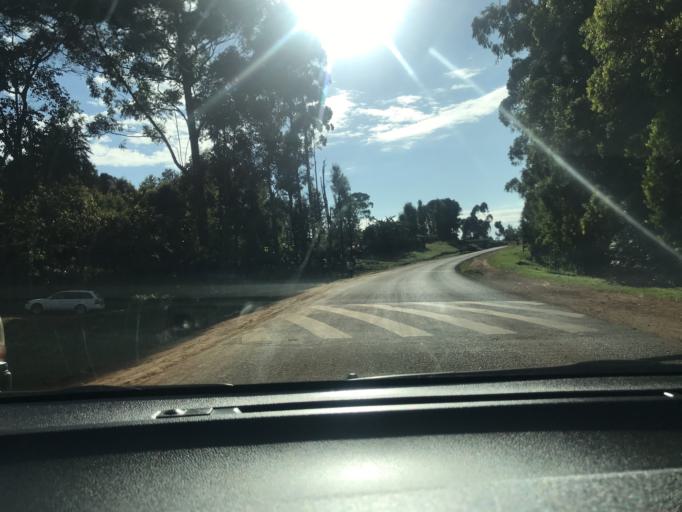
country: KE
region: Kirinyaga
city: Keruguya
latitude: -0.4802
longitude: 37.1768
